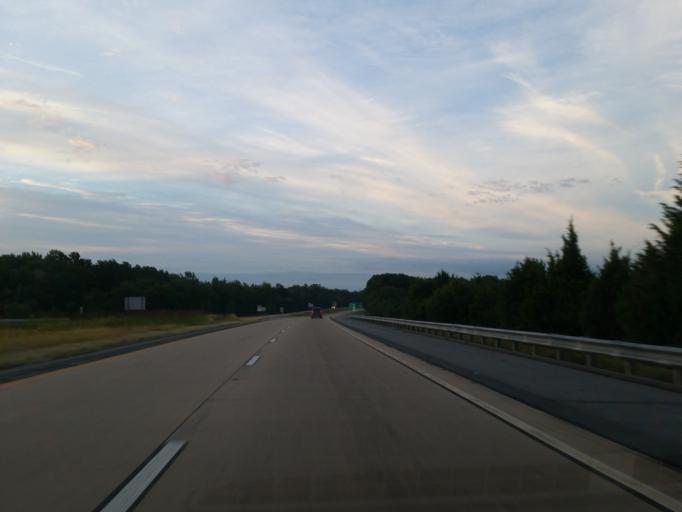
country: US
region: Delaware
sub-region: Kent County
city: Smyrna
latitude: 39.2712
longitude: -75.5819
